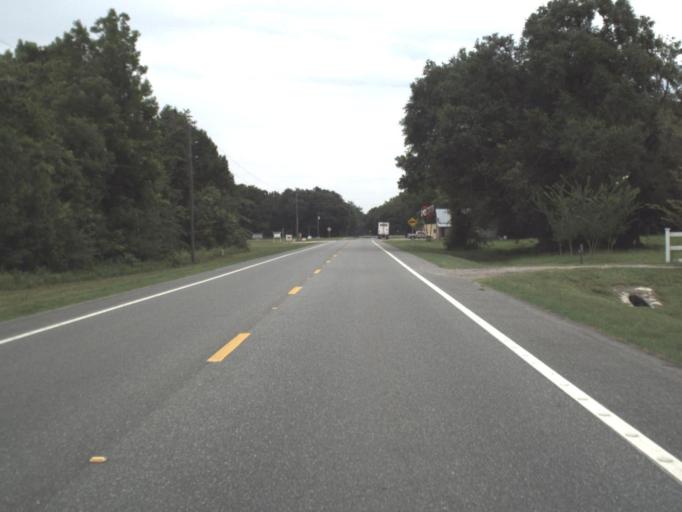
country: US
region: Florida
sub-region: Suwannee County
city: Live Oak
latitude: 30.1371
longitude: -82.9515
